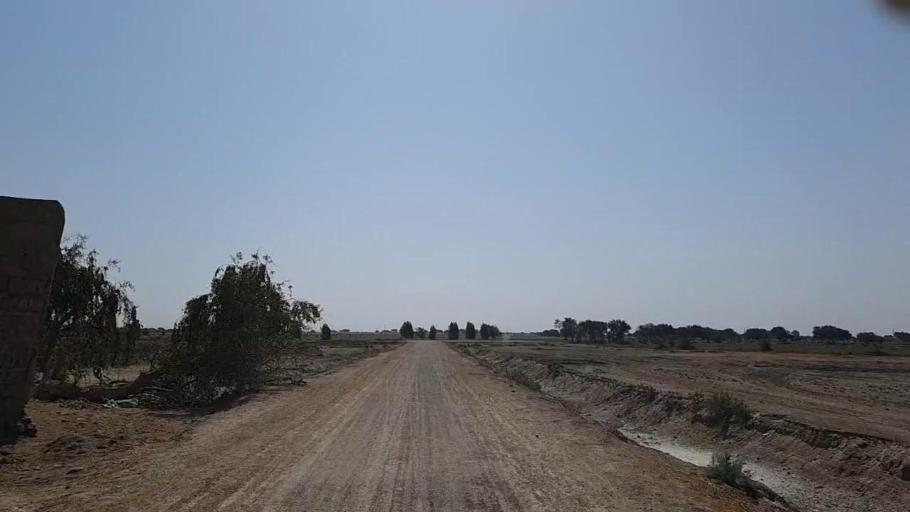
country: PK
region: Sindh
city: Mirpur Batoro
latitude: 24.6826
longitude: 68.2878
